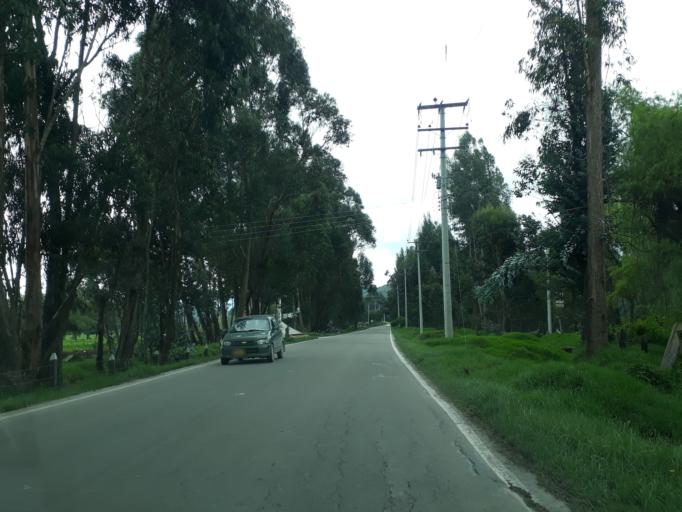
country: CO
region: Cundinamarca
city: Ubate
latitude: 5.3214
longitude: -73.7919
